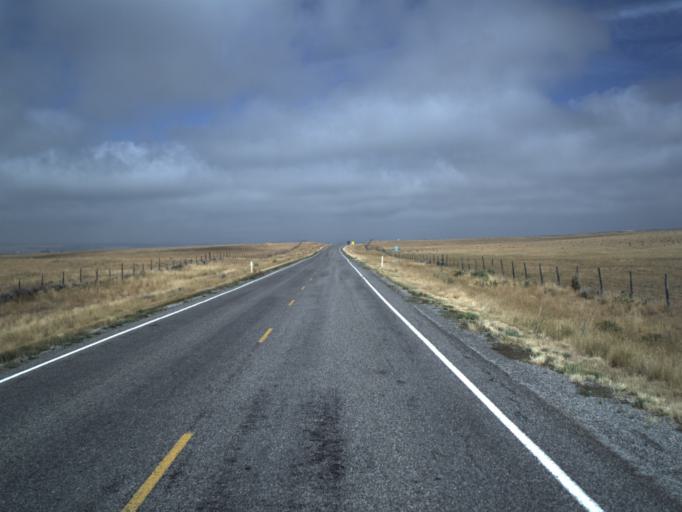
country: US
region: Utah
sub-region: Rich County
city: Randolph
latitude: 41.4567
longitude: -111.0940
